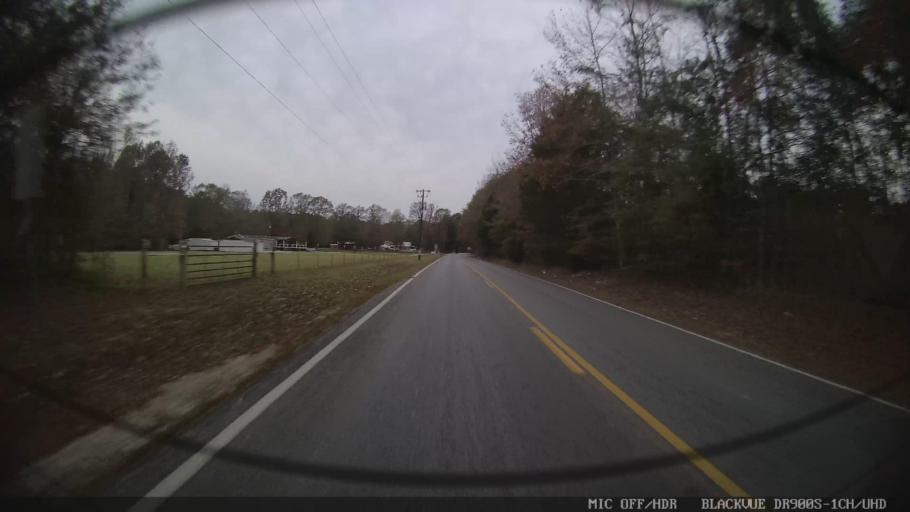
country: US
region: Mississippi
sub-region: Clarke County
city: Stonewall
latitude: 32.0234
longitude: -88.8487
